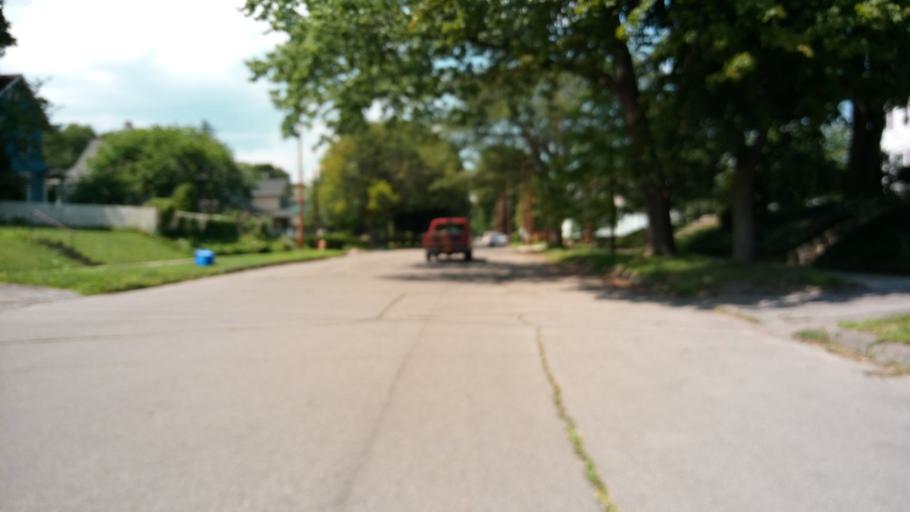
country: US
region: New York
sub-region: Chemung County
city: Elmira
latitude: 42.0889
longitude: -76.8211
